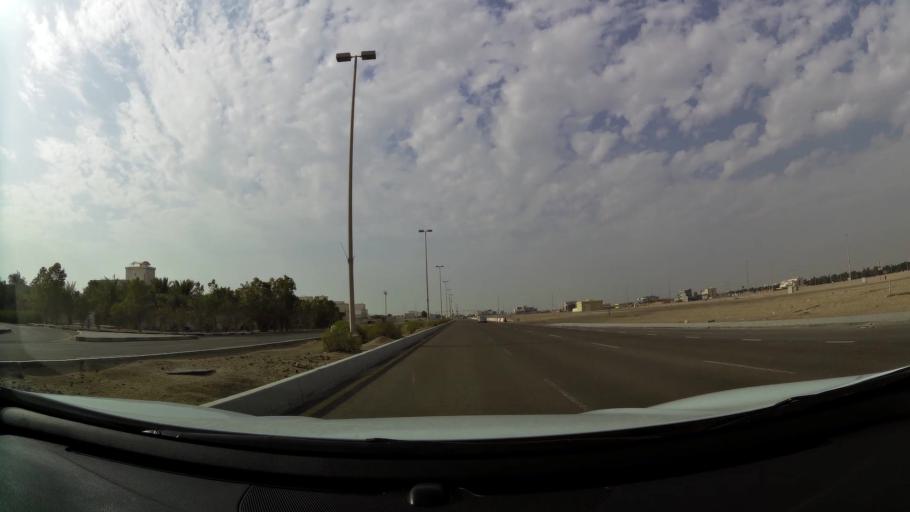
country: AE
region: Abu Dhabi
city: Abu Dhabi
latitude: 24.3359
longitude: 54.5722
